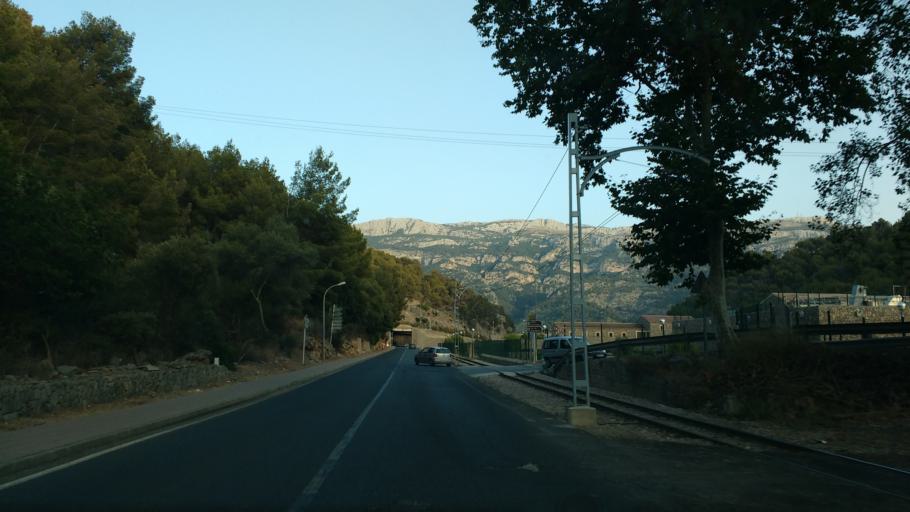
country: ES
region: Balearic Islands
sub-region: Illes Balears
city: Soller
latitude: 39.7867
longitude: 2.6963
